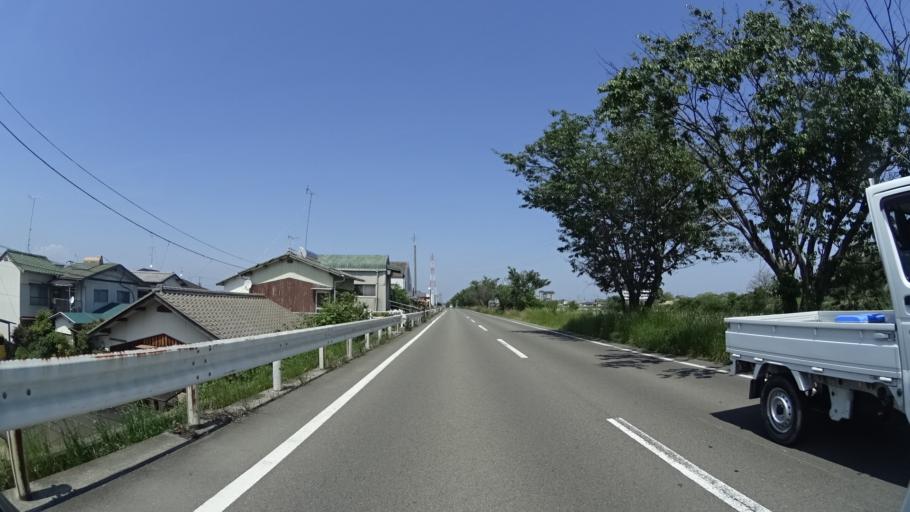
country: JP
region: Ehime
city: Hojo
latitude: 34.0401
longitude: 132.9782
